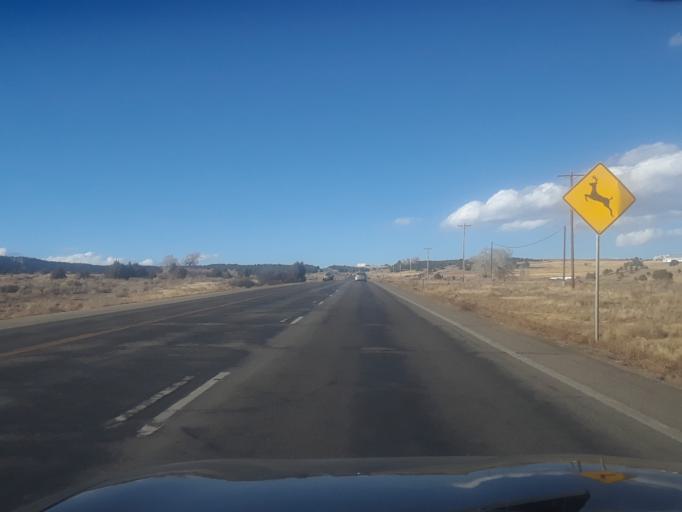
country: US
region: Colorado
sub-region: Chaffee County
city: Salida
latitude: 38.6428
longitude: -106.0832
